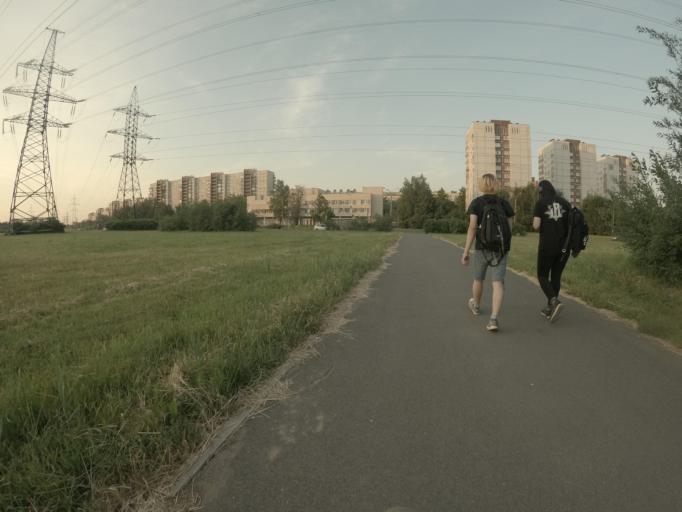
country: RU
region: St.-Petersburg
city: Krasnogvargeisky
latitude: 59.9455
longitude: 30.4604
